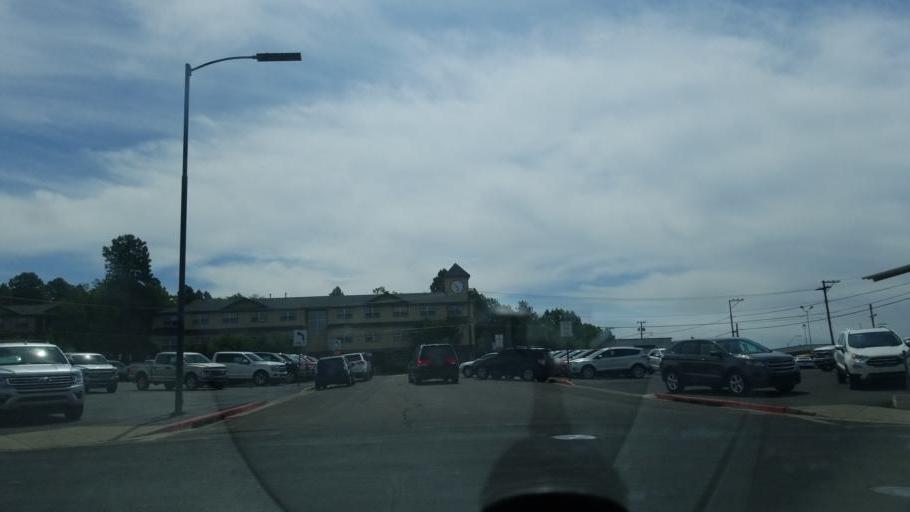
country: US
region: Arizona
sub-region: Coconino County
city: Flagstaff
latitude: 35.1975
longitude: -111.6455
